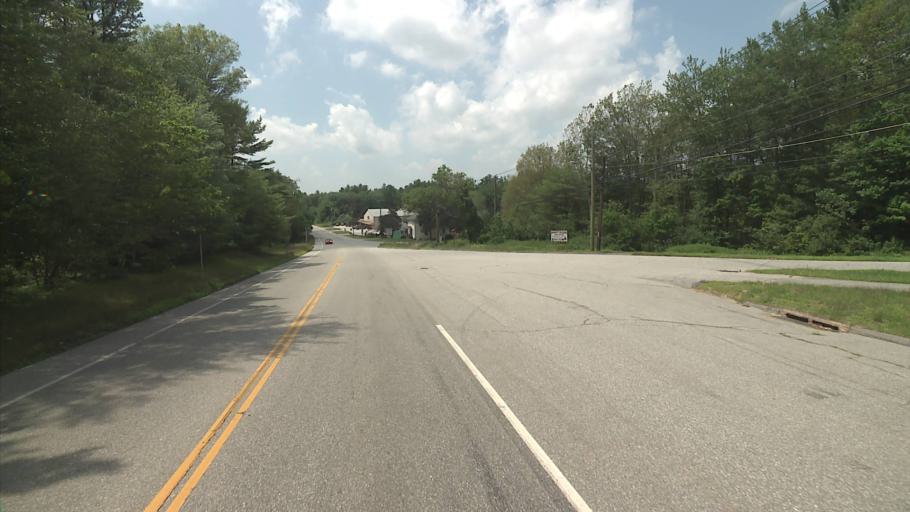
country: US
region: Connecticut
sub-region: Windham County
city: Plainfield
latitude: 41.5763
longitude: -71.8533
